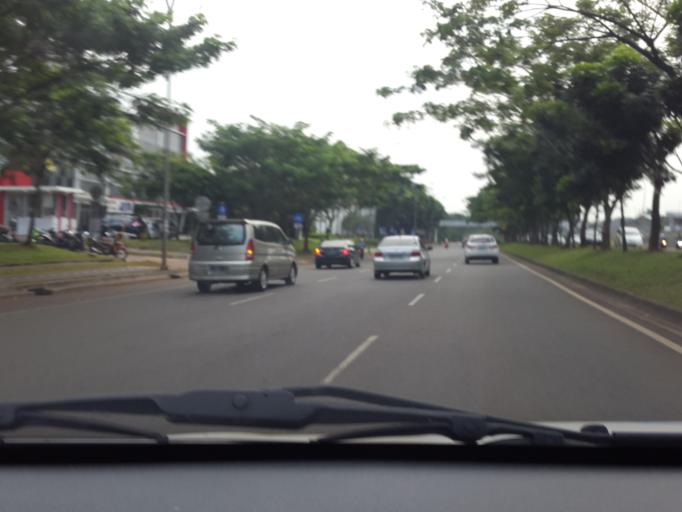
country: ID
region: Banten
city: South Tangerang
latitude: -6.2735
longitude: 106.7111
